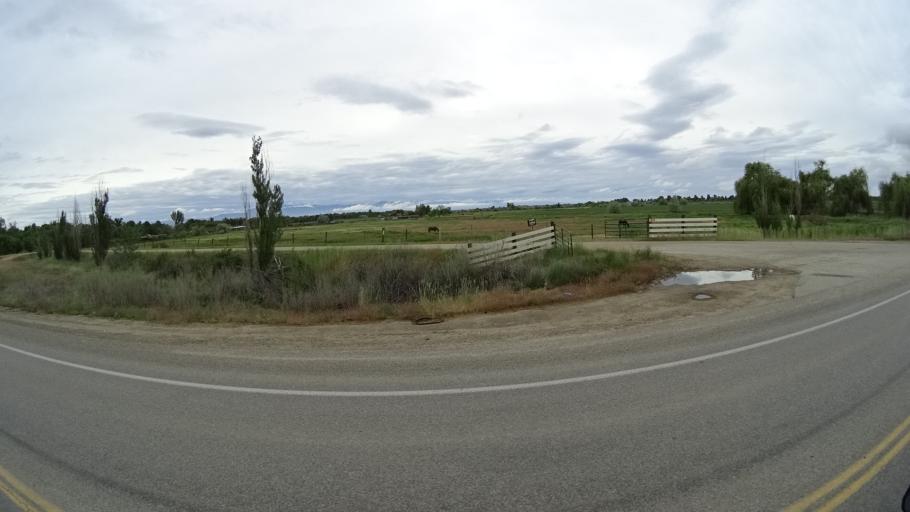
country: US
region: Idaho
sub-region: Ada County
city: Star
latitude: 43.6780
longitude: -116.4935
